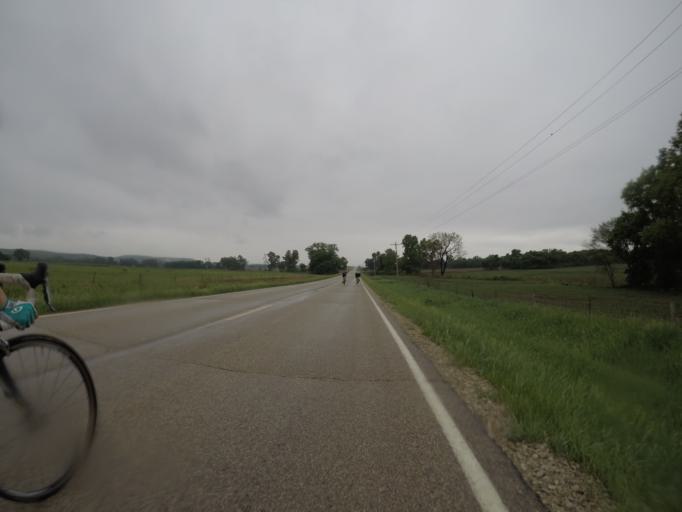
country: US
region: Kansas
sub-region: Pottawatomie County
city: Wamego
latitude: 39.3713
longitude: -96.2212
